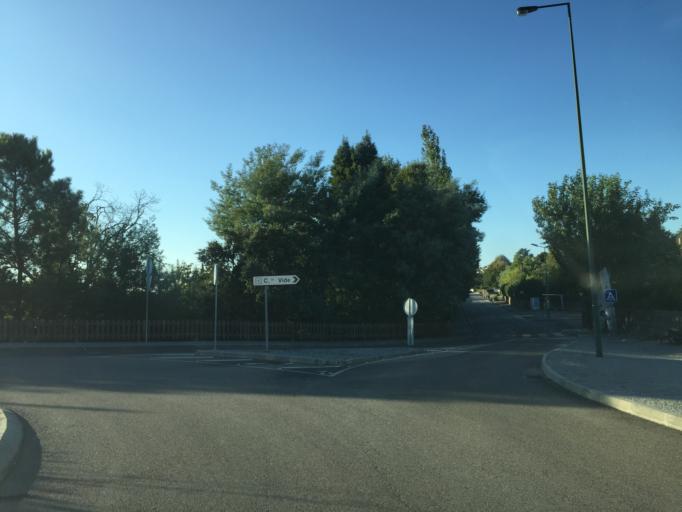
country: PT
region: Portalegre
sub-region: Castelo de Vide
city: Castelo de Vide
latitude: 39.4063
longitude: -7.4451
